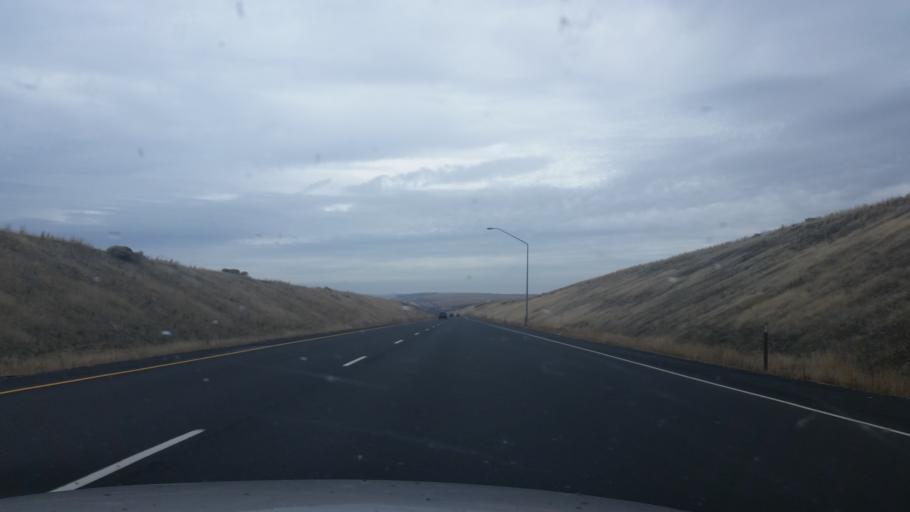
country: US
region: Washington
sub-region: Grant County
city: Warden
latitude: 47.0869
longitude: -118.8553
